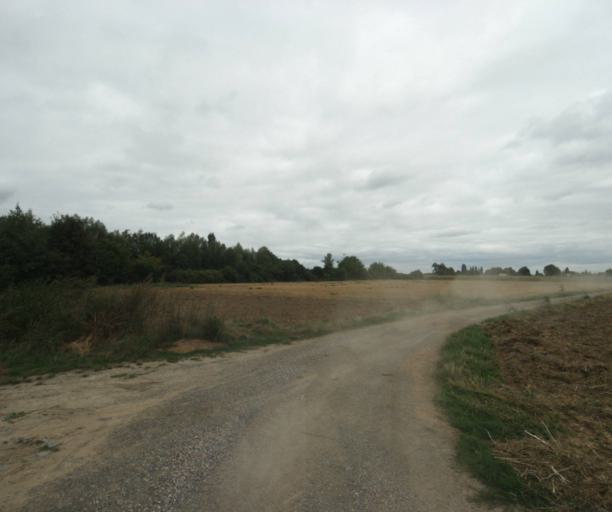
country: FR
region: Nord-Pas-de-Calais
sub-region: Departement du Nord
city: Fretin
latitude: 50.5597
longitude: 3.1265
